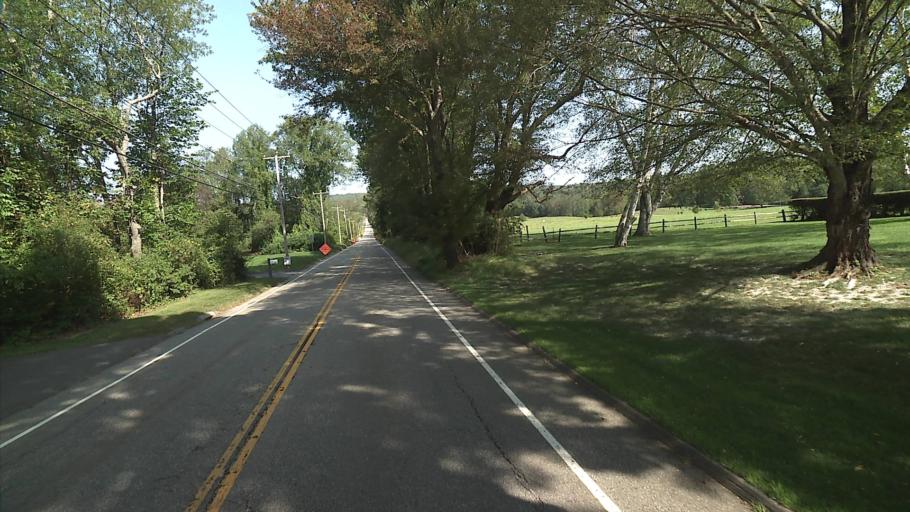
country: US
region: Connecticut
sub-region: Windham County
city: Putnam
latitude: 41.8517
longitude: -71.9590
